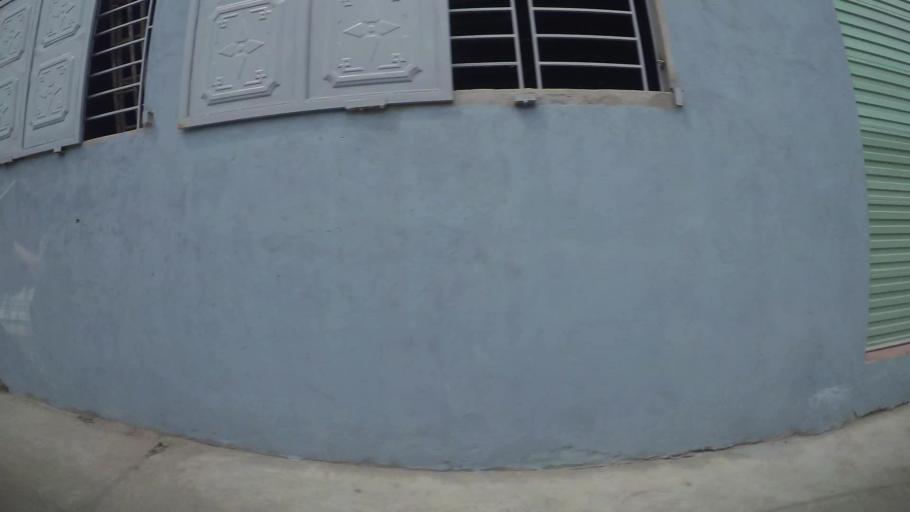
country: VN
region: Ha Noi
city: Trau Quy
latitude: 21.0523
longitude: 105.9236
